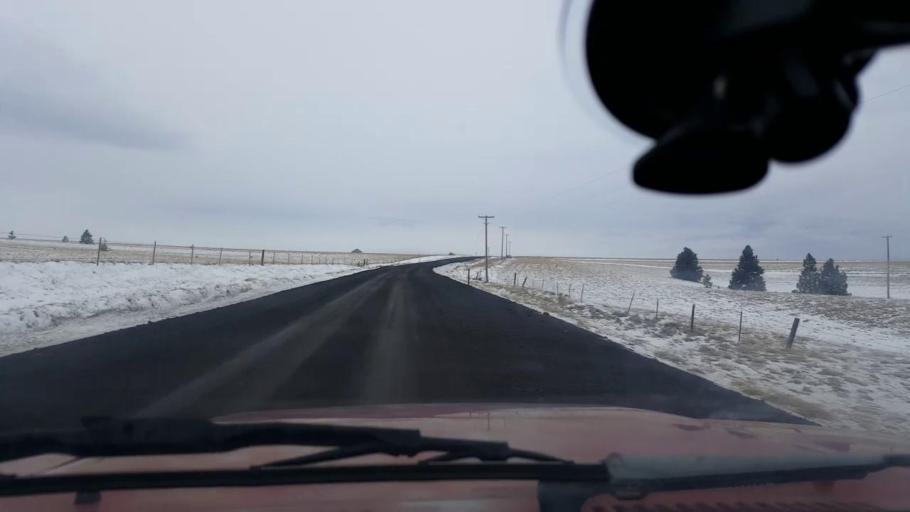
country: US
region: Washington
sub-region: Garfield County
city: Pomeroy
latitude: 46.3196
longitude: -117.4040
